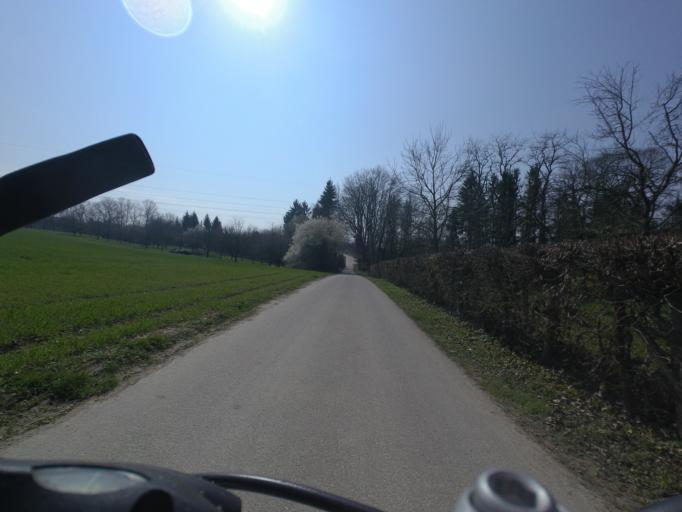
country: DE
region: Baden-Wuerttemberg
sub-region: Regierungsbezirk Stuttgart
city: Unterensingen
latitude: 48.6614
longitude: 9.3665
